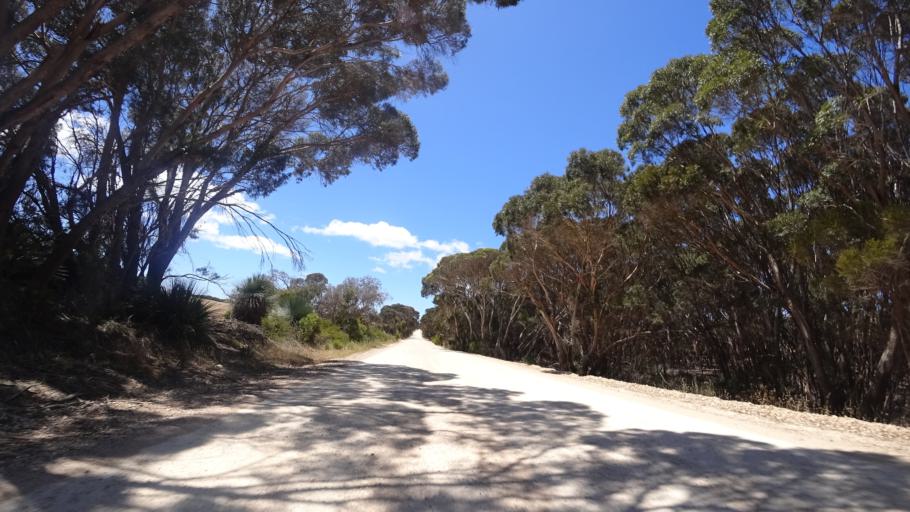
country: AU
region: South Australia
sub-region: Kangaroo Island
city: Kingscote
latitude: -35.8266
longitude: 138.0000
